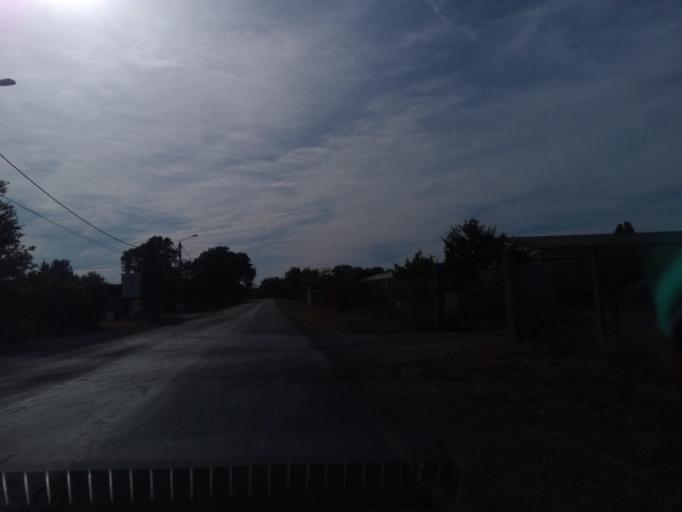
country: FR
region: Poitou-Charentes
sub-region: Departement de la Vienne
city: Montmorillon
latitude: 46.4301
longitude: 0.8986
